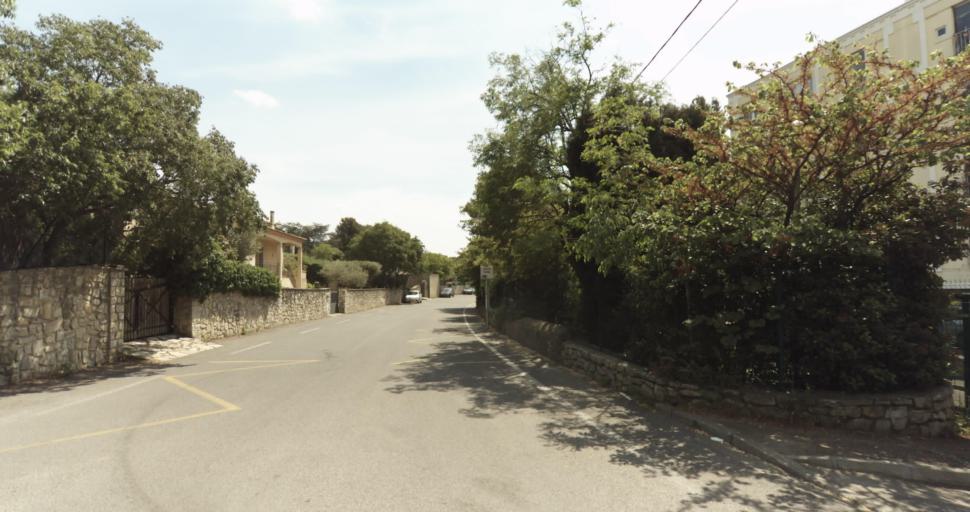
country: FR
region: Languedoc-Roussillon
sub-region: Departement du Gard
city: Nimes
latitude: 43.8494
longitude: 4.3846
